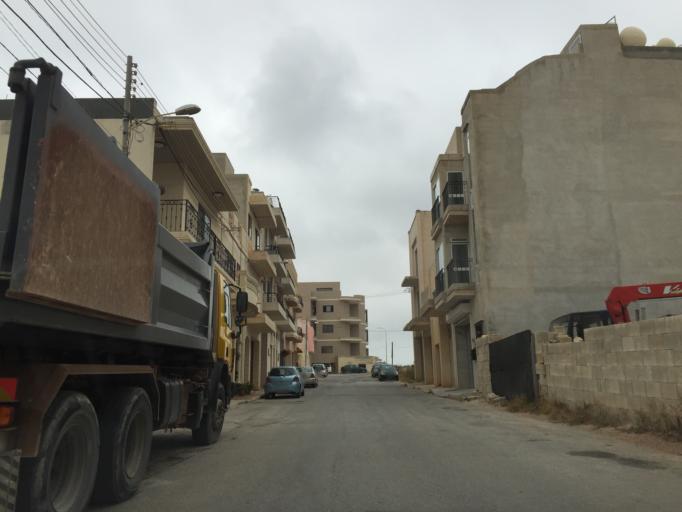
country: MT
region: L-Imgarr
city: Imgarr
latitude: 35.9218
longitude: 14.3683
